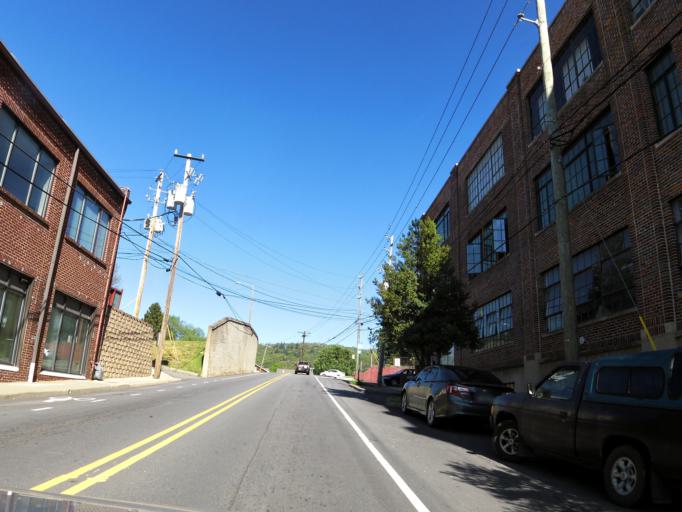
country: US
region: North Carolina
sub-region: Buncombe County
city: Asheville
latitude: 35.5910
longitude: -82.5549
